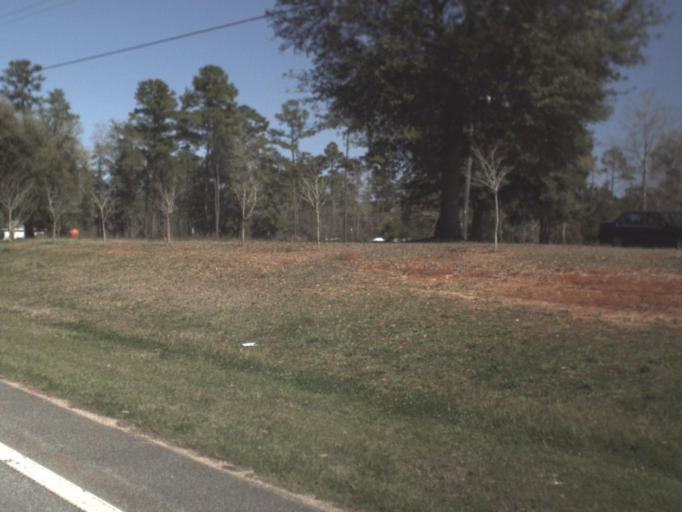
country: US
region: Florida
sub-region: Gadsden County
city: Quincy
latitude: 30.6383
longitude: -84.5999
